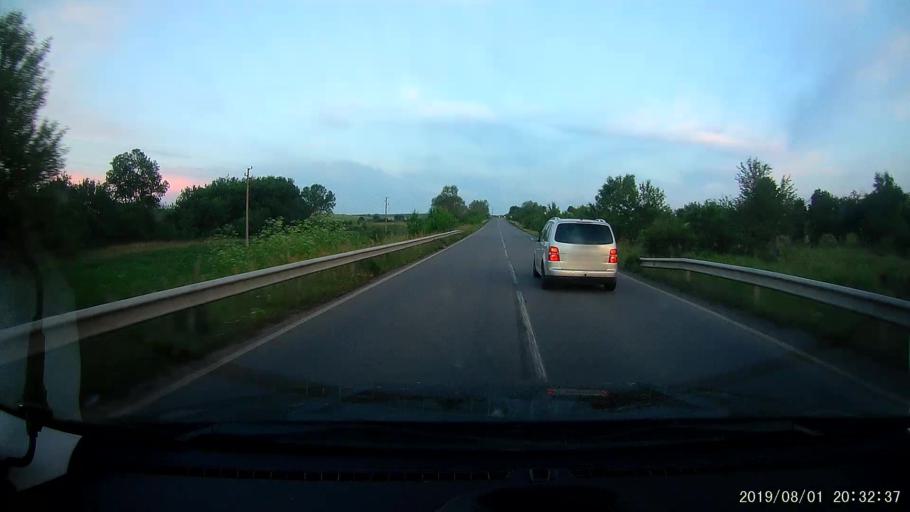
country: BG
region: Yambol
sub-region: Obshtina Elkhovo
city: Elkhovo
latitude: 42.1195
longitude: 26.5299
